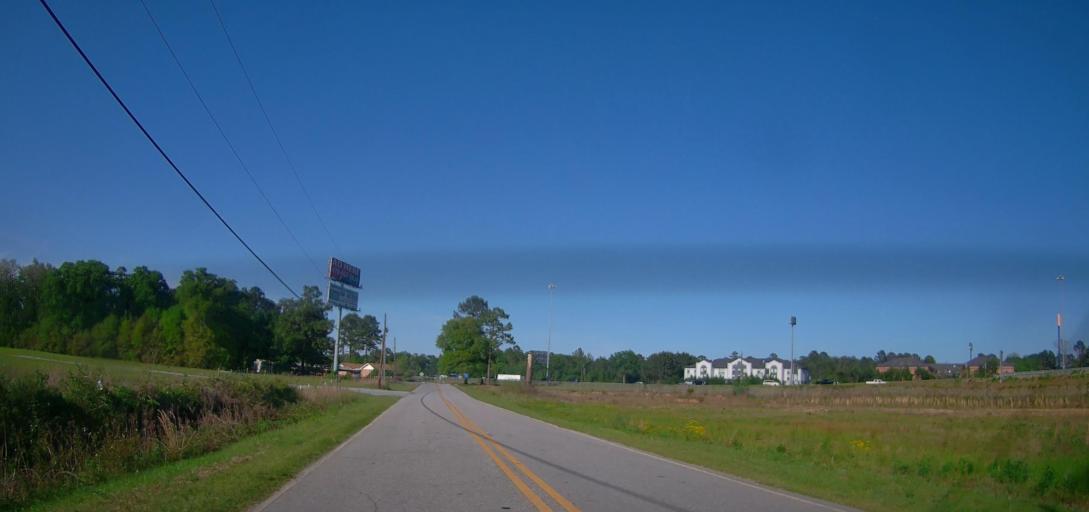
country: US
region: Georgia
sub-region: Houston County
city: Perry
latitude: 32.4484
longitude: -83.7561
